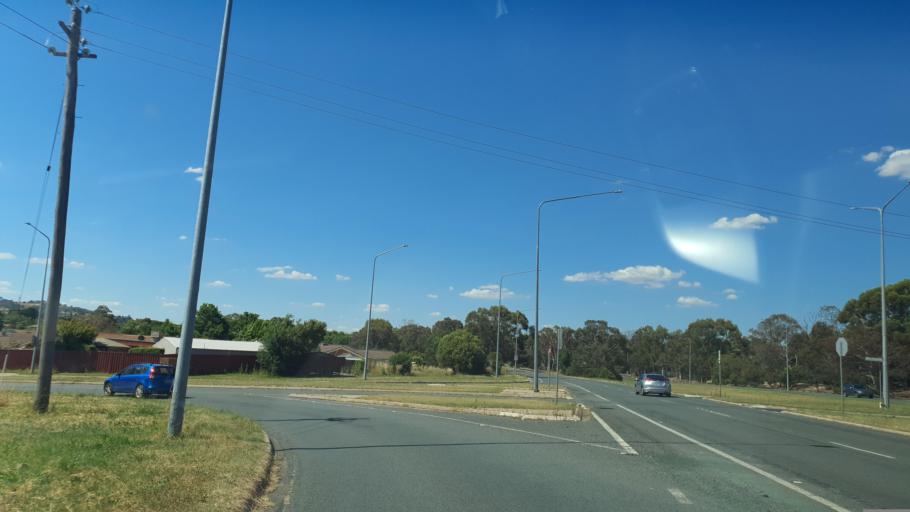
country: AU
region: Australian Capital Territory
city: Belconnen
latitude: -35.2265
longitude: 149.0604
